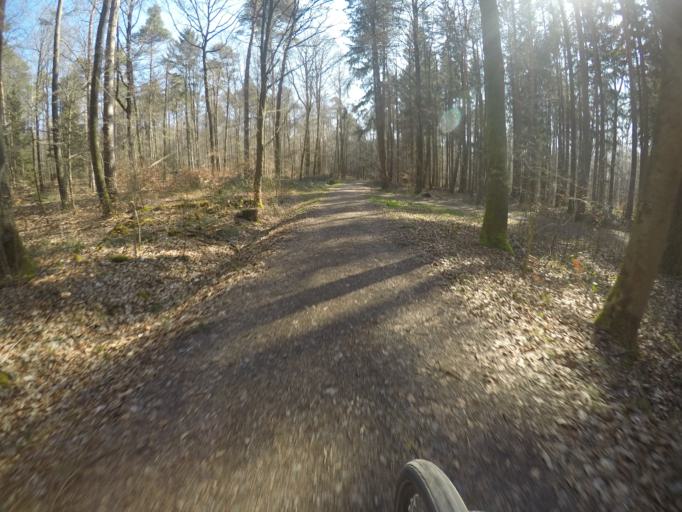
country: DE
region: Baden-Wuerttemberg
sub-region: Regierungsbezirk Stuttgart
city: Stuttgart Feuerbach
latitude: 48.7608
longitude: 9.1197
